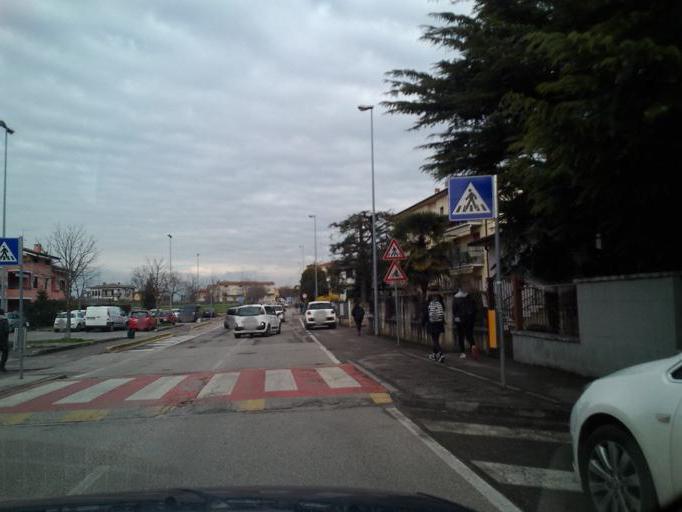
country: IT
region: Veneto
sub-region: Provincia di Verona
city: Villafranca di Verona
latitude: 45.3584
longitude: 10.8394
